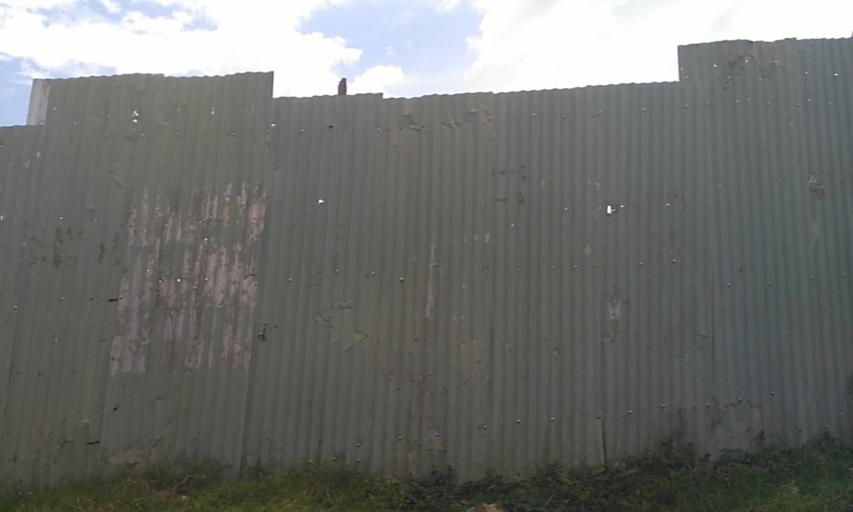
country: UG
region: Central Region
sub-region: Kampala District
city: Kampala
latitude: 0.3333
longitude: 32.6077
